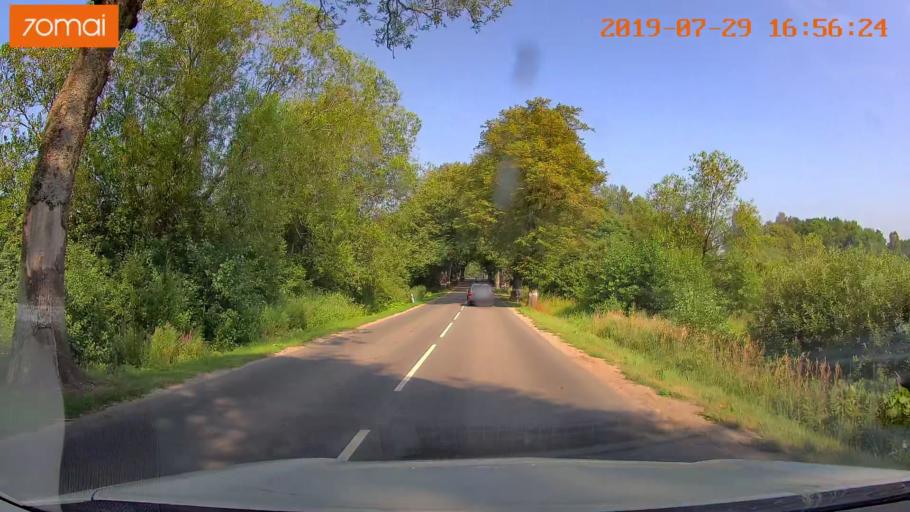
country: RU
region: Kaliningrad
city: Volochayevskoye
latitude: 54.8148
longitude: 20.1699
